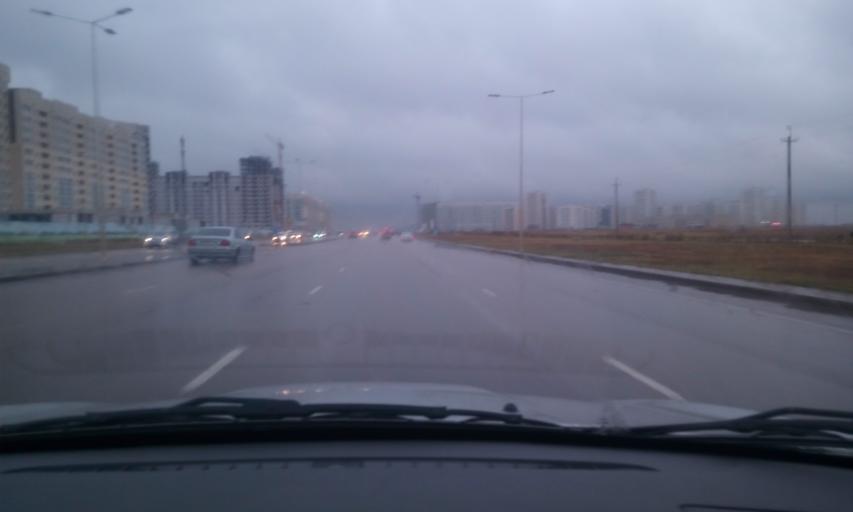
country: KZ
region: Astana Qalasy
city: Astana
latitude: 51.1303
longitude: 71.3797
